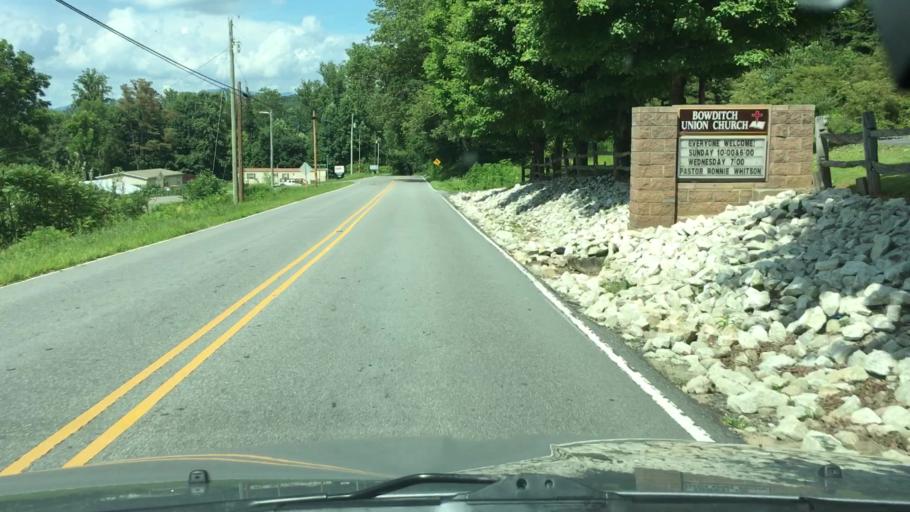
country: US
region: North Carolina
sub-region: Yancey County
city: Burnsville
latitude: 35.8831
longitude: -82.2167
